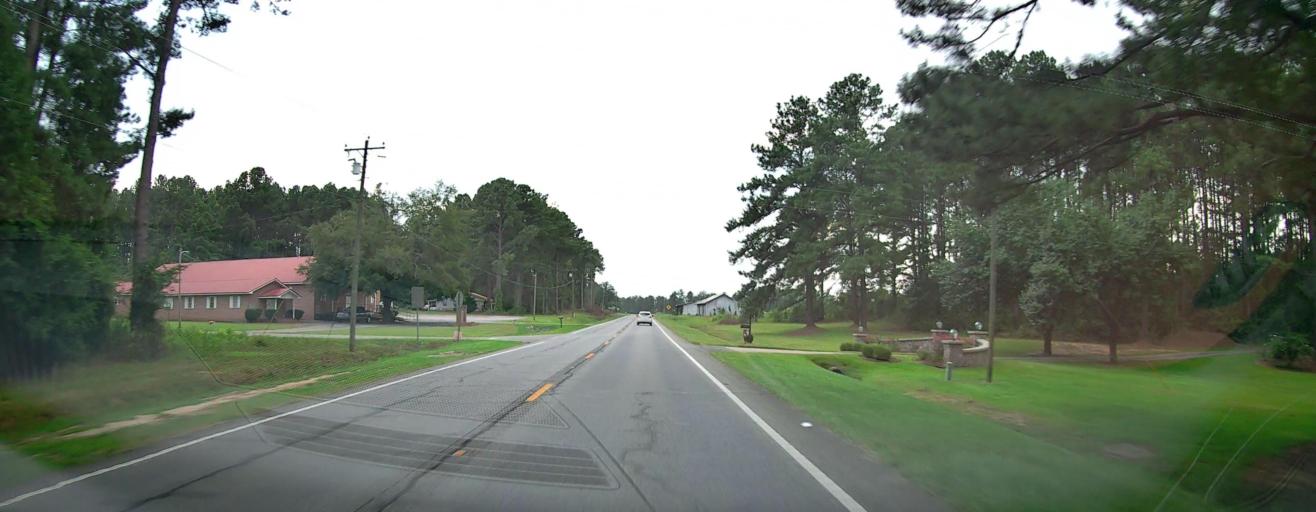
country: US
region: Georgia
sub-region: Laurens County
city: East Dublin
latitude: 32.5829
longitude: -82.8354
